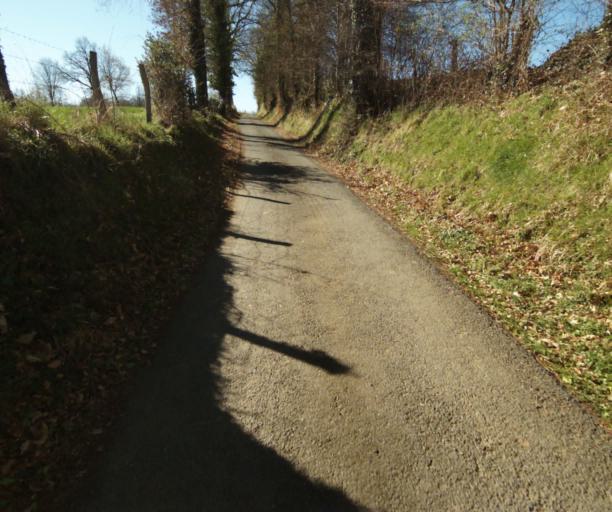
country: FR
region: Limousin
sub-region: Departement de la Correze
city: Chamboulive
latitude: 45.4106
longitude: 1.6974
